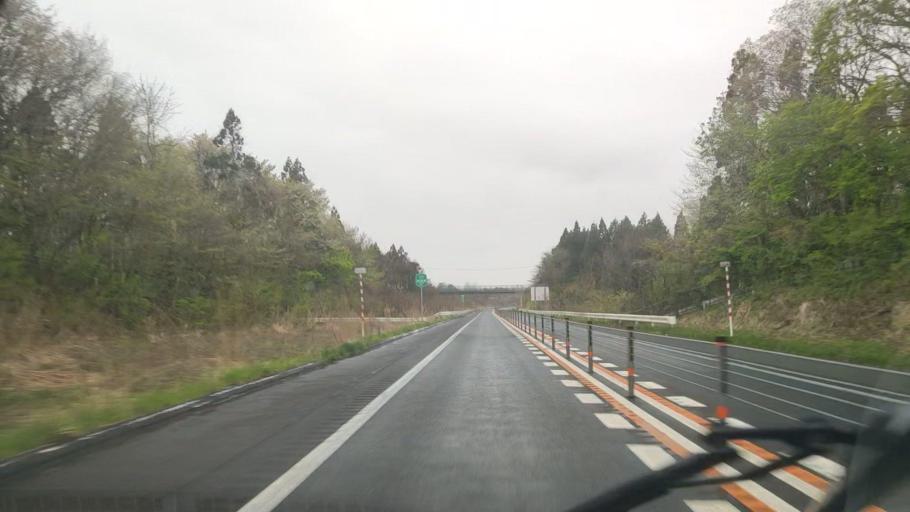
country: JP
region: Akita
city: Noshiromachi
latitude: 40.1477
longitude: 140.0207
